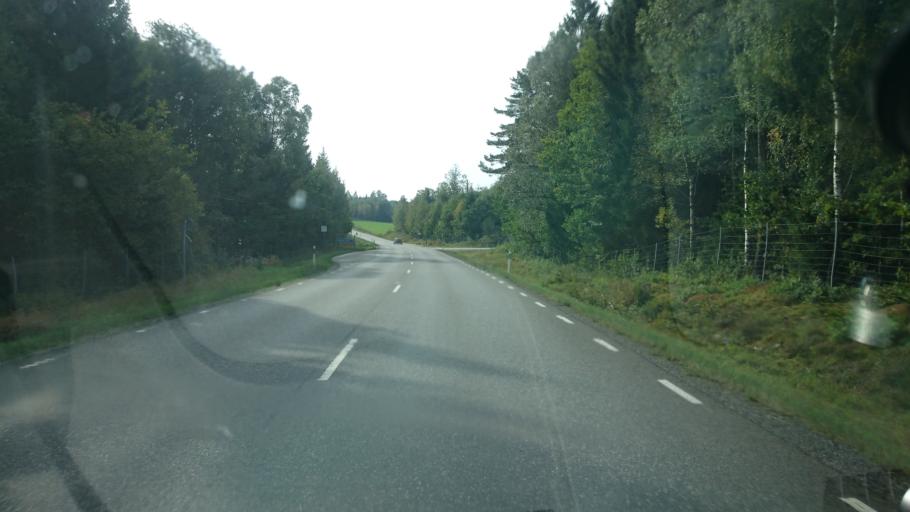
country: SE
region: Vaestra Goetaland
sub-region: Alingsas Kommun
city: Alingsas
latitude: 58.0072
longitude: 12.4444
